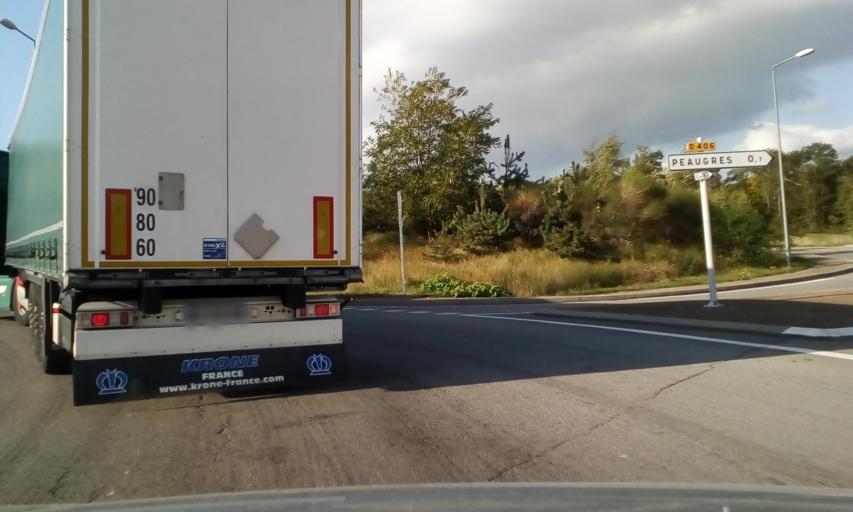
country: FR
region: Rhone-Alpes
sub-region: Departement de l'Ardeche
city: Peaugres
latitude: 45.2862
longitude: 4.7252
